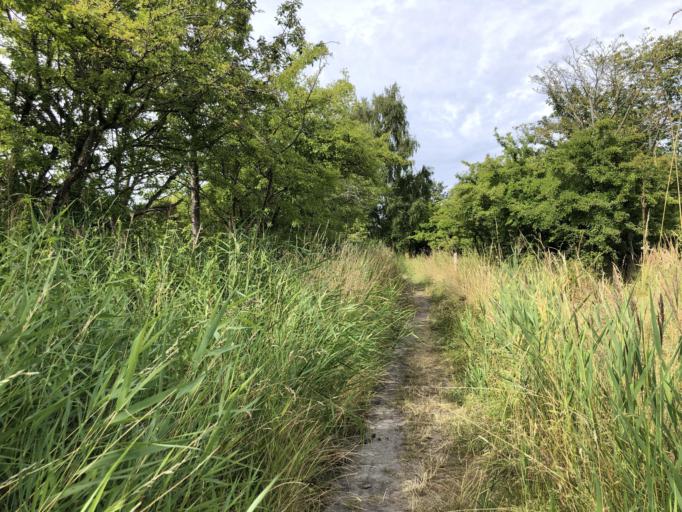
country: DK
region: Capital Region
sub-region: Kobenhavn
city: Christianshavn
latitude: 55.6567
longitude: 12.5807
